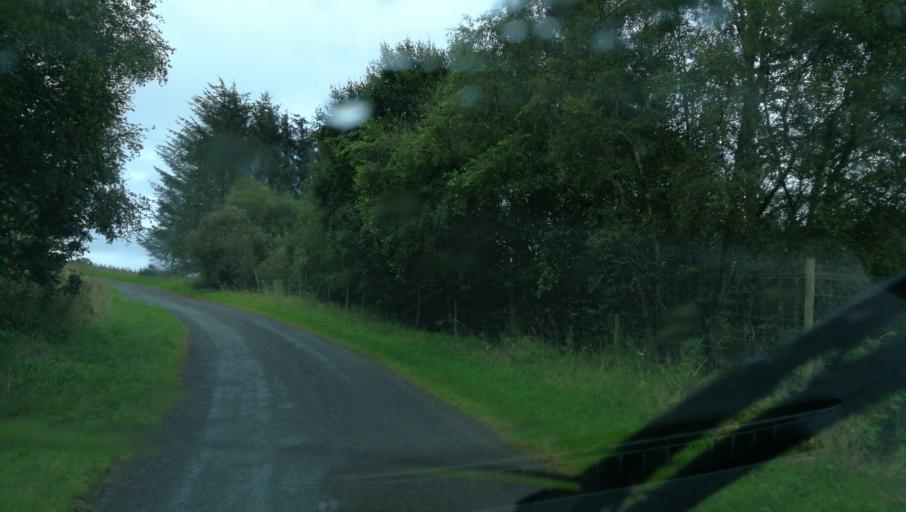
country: GB
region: Scotland
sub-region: Perth and Kinross
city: Blairgowrie
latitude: 56.6905
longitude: -3.4009
